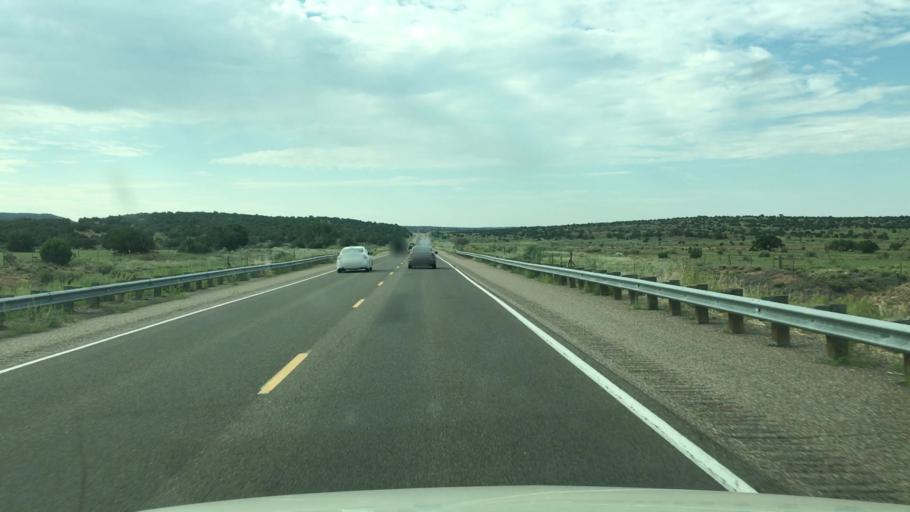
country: US
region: New Mexico
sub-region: Santa Fe County
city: Eldorado at Santa Fe
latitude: 35.3070
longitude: -105.8288
